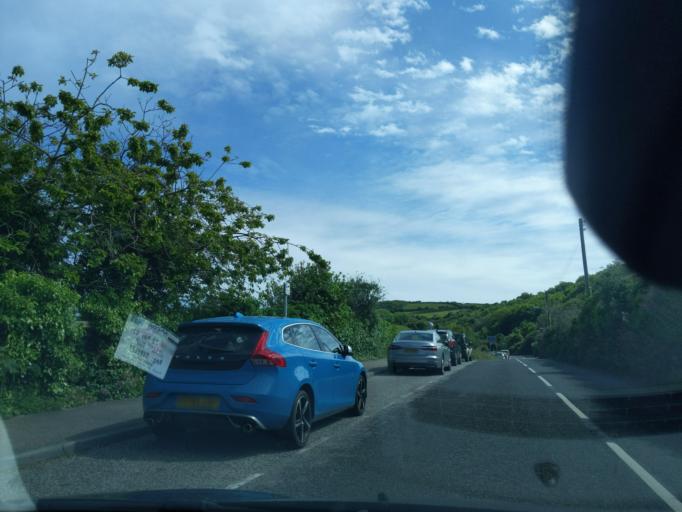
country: GB
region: England
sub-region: Cornwall
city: Penzance
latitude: 50.0955
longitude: -5.5390
